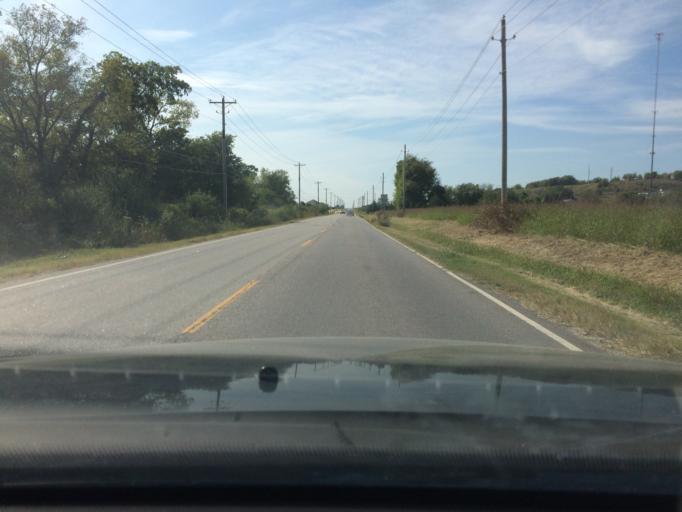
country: US
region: Oklahoma
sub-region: Tulsa County
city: Broken Arrow
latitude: 36.1045
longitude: -95.7809
